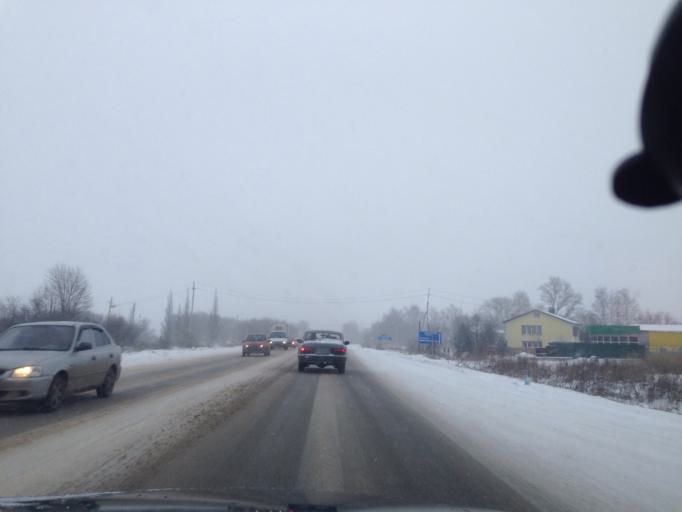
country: RU
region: Tula
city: Bolokhovo
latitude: 54.0683
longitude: 37.7965
